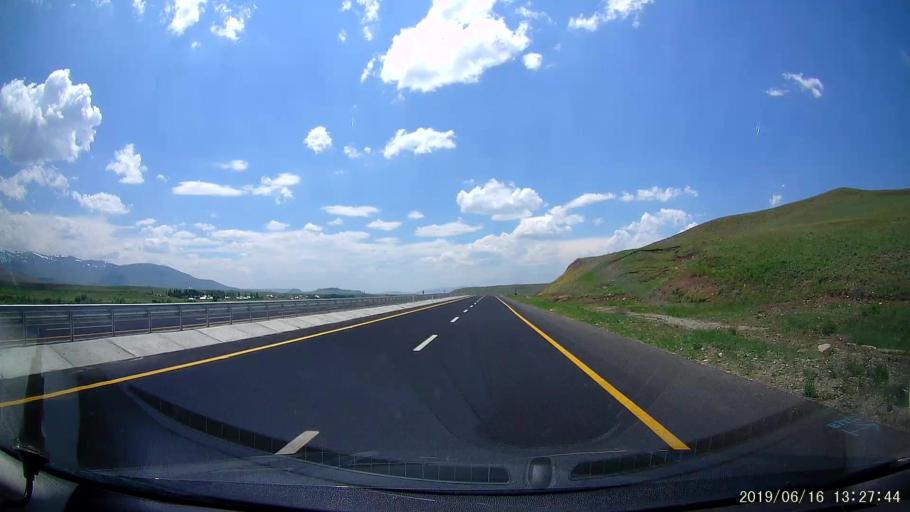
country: TR
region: Agri
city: Murat
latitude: 39.6715
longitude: 43.3034
